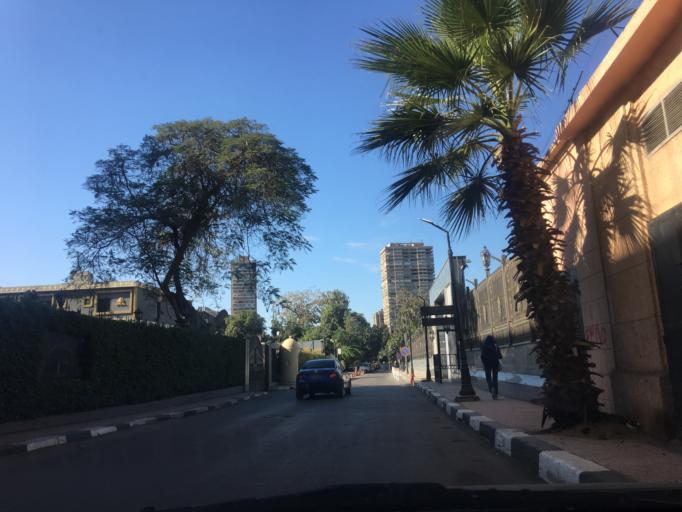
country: EG
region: Muhafazat al Qahirah
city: Cairo
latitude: 30.0466
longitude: 31.2235
